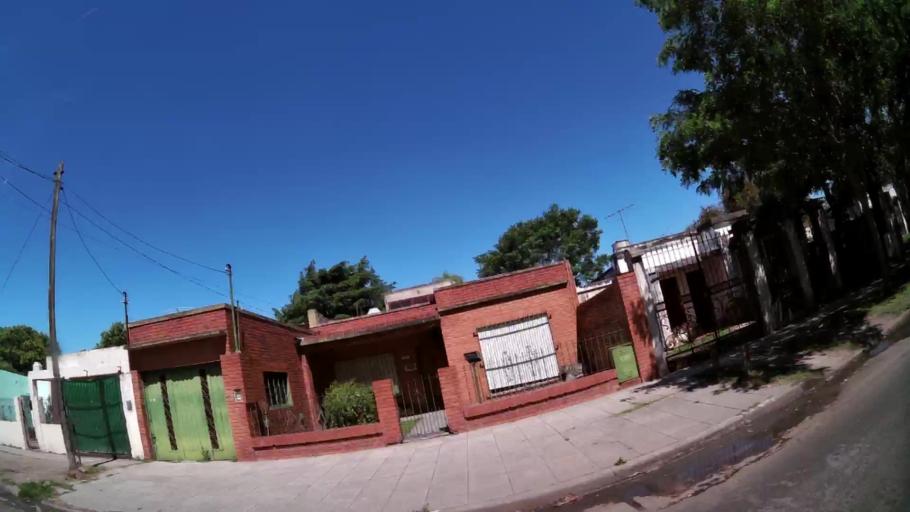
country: AR
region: Buenos Aires
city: Hurlingham
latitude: -34.5104
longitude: -58.6752
